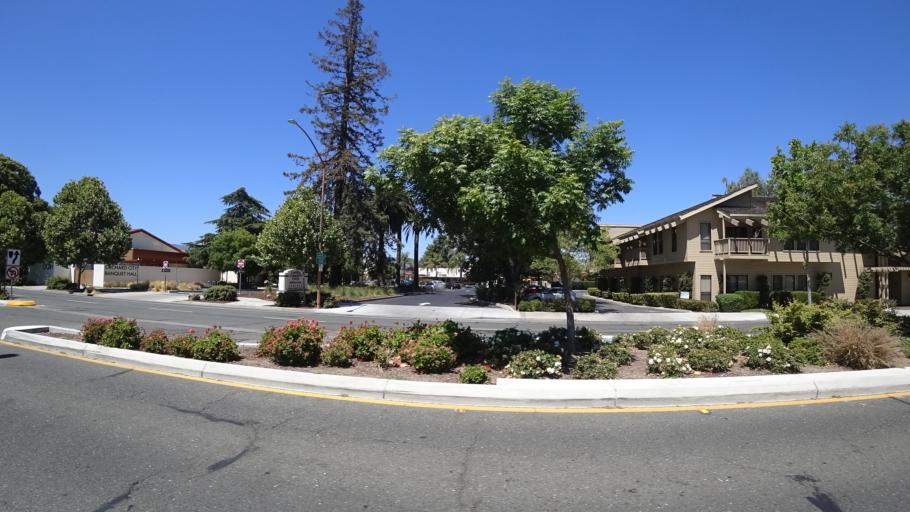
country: US
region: California
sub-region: Santa Clara County
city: Campbell
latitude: 37.2887
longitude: -121.9498
